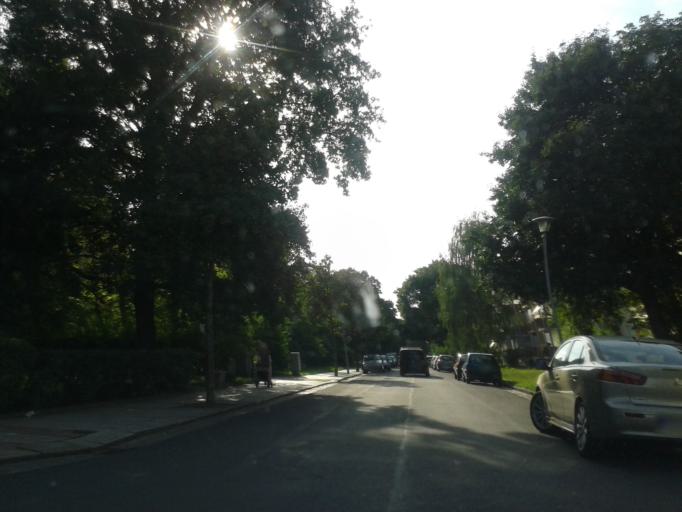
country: DE
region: Saxony
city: Dresden
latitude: 51.0523
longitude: 13.7570
